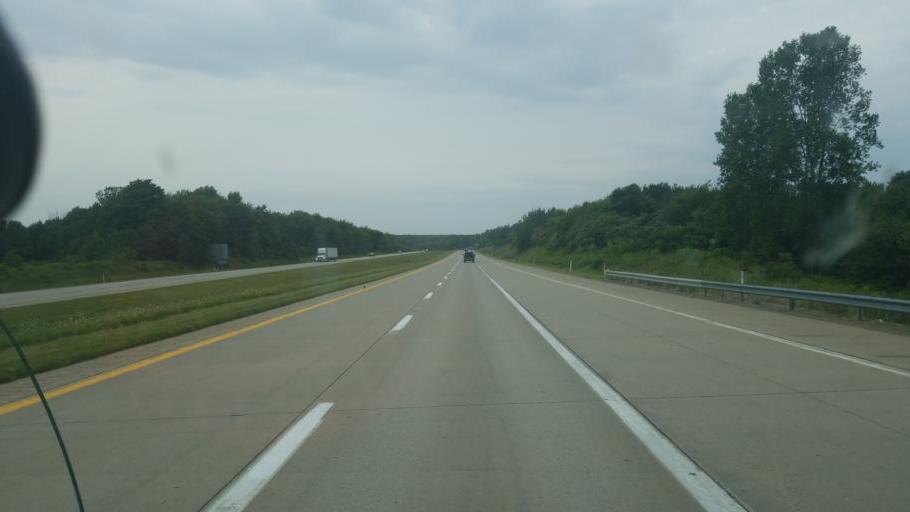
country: US
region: Pennsylvania
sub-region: Erie County
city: North East
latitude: 42.1407
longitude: -79.8270
